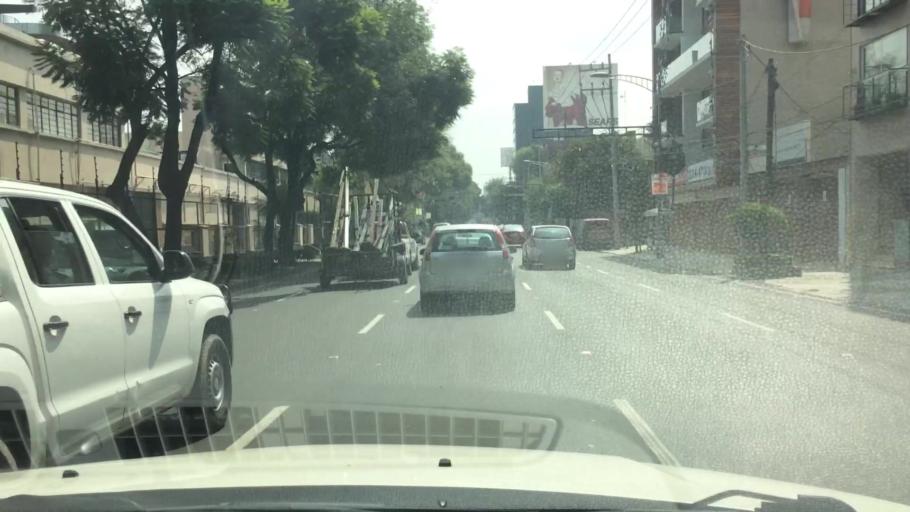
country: MX
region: Mexico City
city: Colonia del Valle
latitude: 19.3822
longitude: -99.1634
